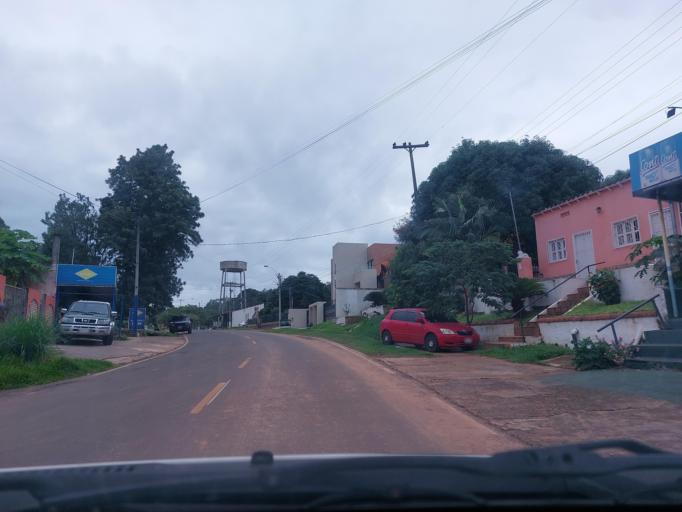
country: PY
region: San Pedro
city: Guayaybi
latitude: -24.6578
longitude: -56.4388
